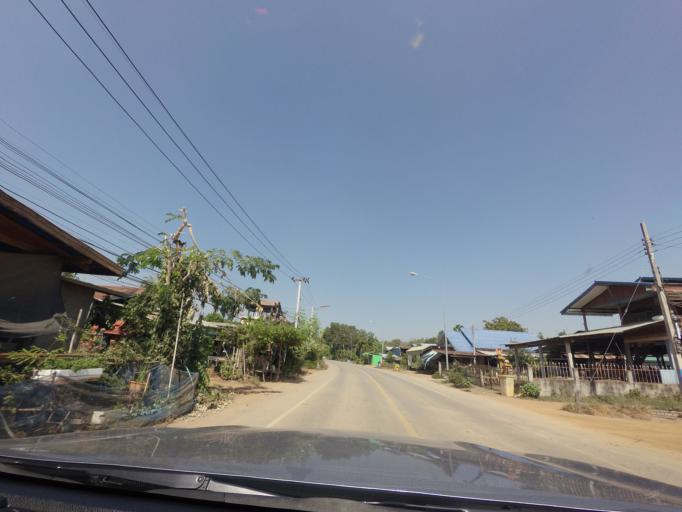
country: TH
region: Sukhothai
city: Si Samrong
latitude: 17.2255
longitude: 99.7757
